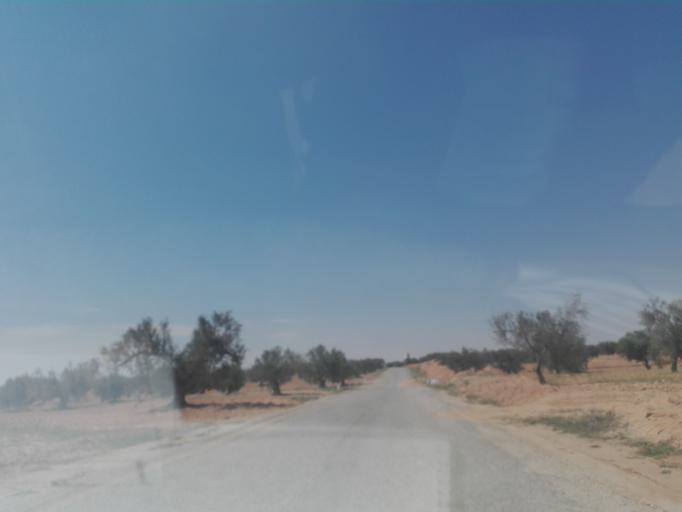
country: TN
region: Safaqis
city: Bi'r `Ali Bin Khalifah
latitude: 34.6279
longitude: 10.3740
